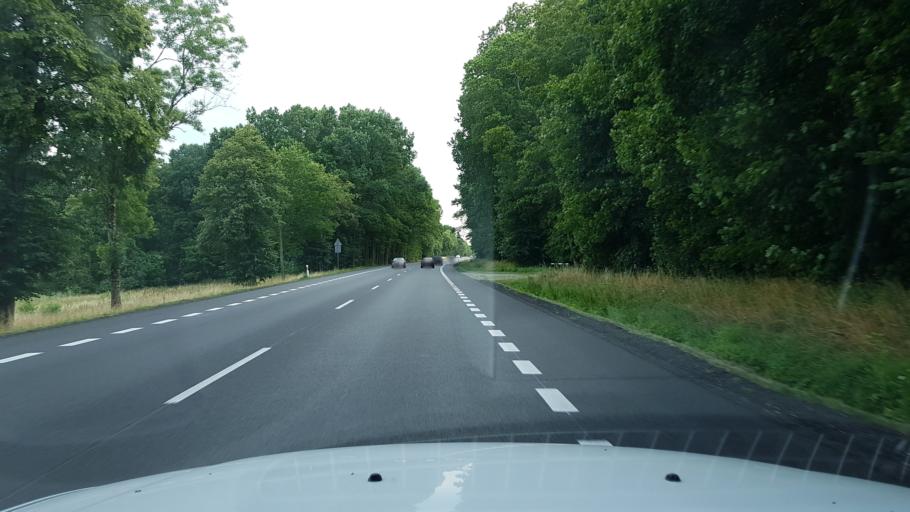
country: PL
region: West Pomeranian Voivodeship
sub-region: Powiat bialogardzki
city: Bialogard
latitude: 54.1036
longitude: 15.9963
